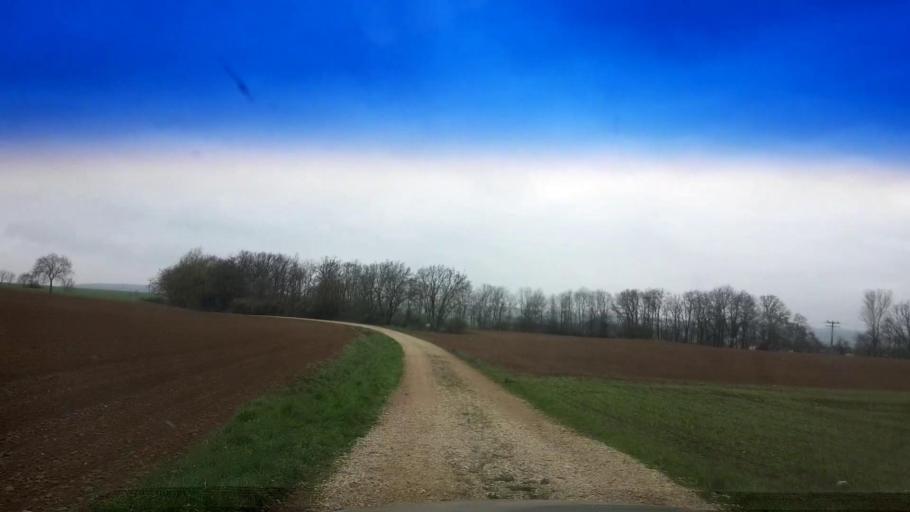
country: DE
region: Bavaria
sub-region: Upper Franconia
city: Schesslitz
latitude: 49.9523
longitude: 11.0227
